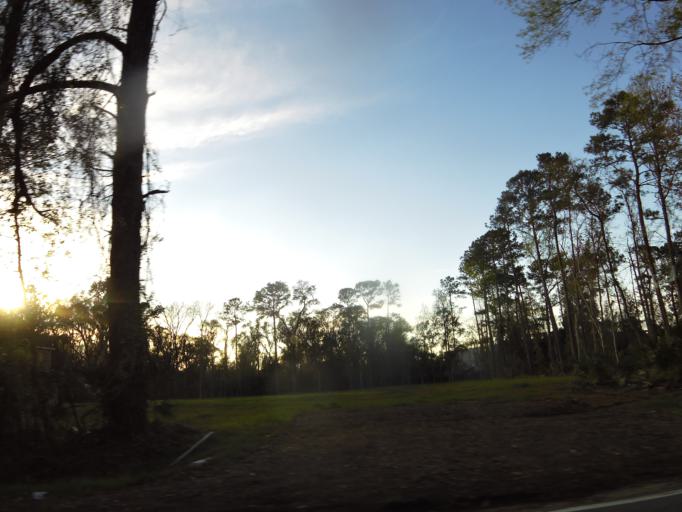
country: US
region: Florida
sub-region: Duval County
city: Jacksonville
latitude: 30.4702
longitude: -81.6550
